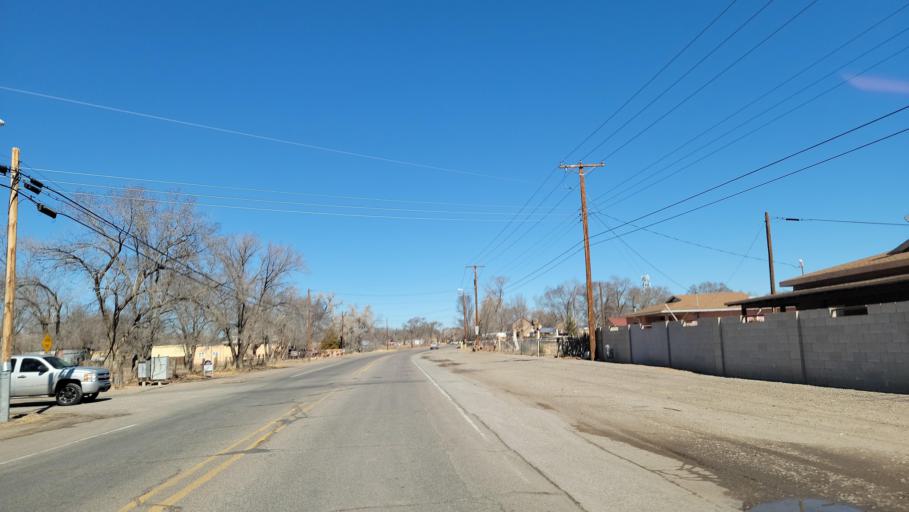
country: US
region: New Mexico
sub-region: Bernalillo County
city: South Valley
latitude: 34.9819
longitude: -106.6971
